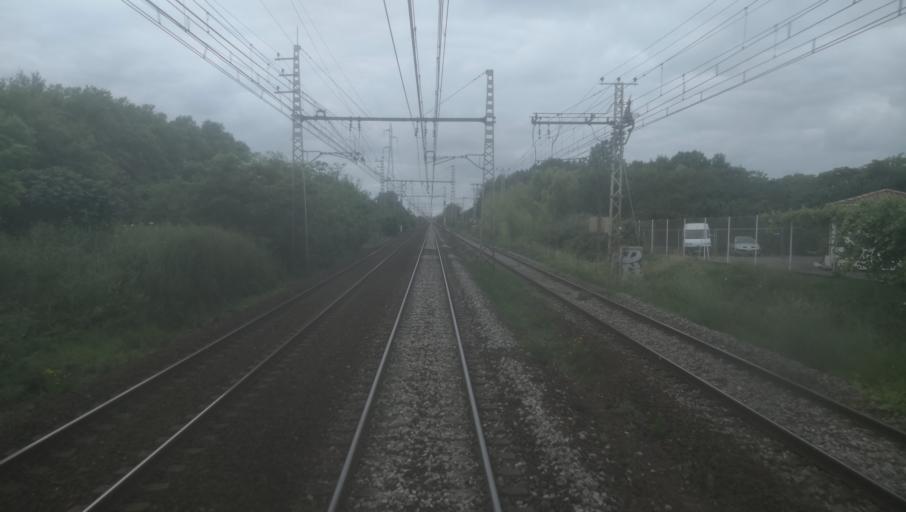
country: FR
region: Midi-Pyrenees
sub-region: Departement de la Haute-Garonne
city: Aucamville
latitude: 43.6705
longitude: 1.4092
